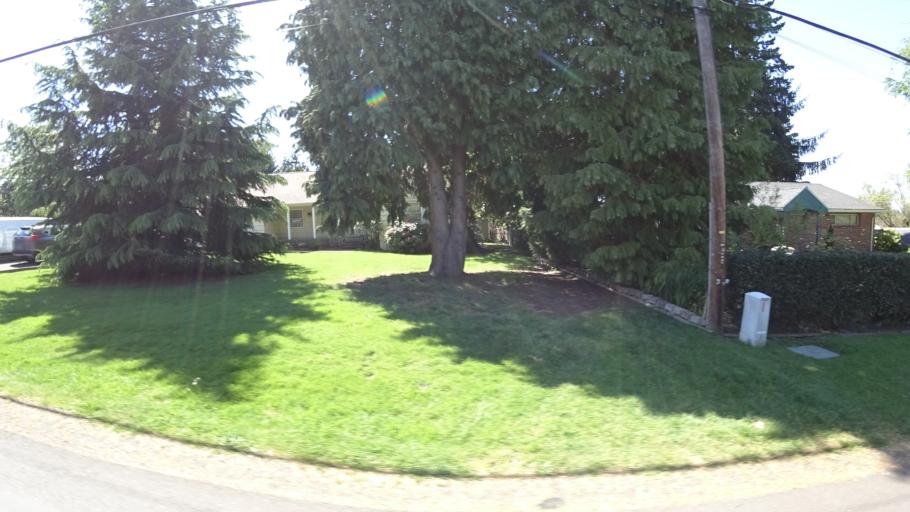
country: US
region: Oregon
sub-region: Washington County
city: Aloha
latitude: 45.4806
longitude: -122.8493
